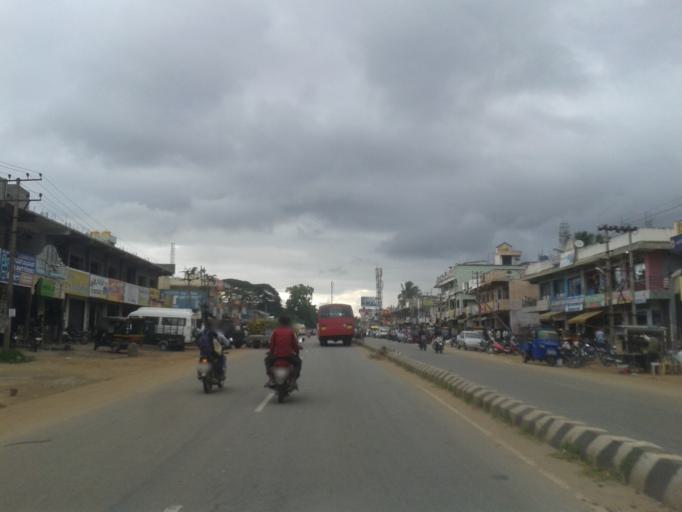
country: IN
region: Karnataka
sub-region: Hassan
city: Channarayapatna
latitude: 12.8985
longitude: 76.3936
